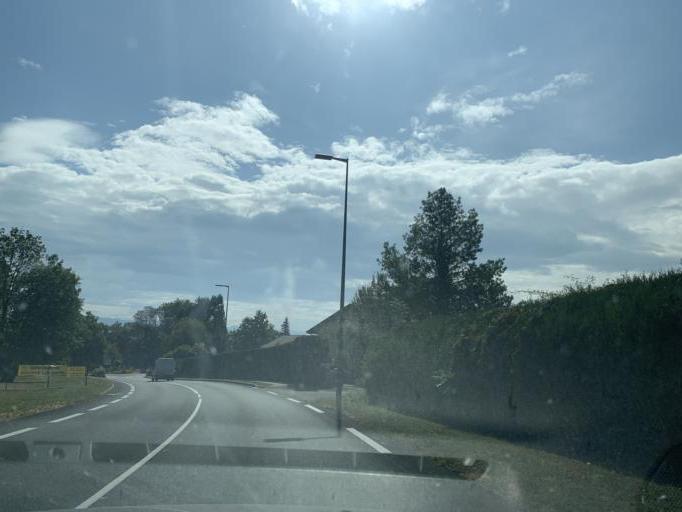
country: FR
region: Rhone-Alpes
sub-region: Departement de l'Ain
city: Divonne-les-Bains
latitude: 46.3510
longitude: 6.1308
